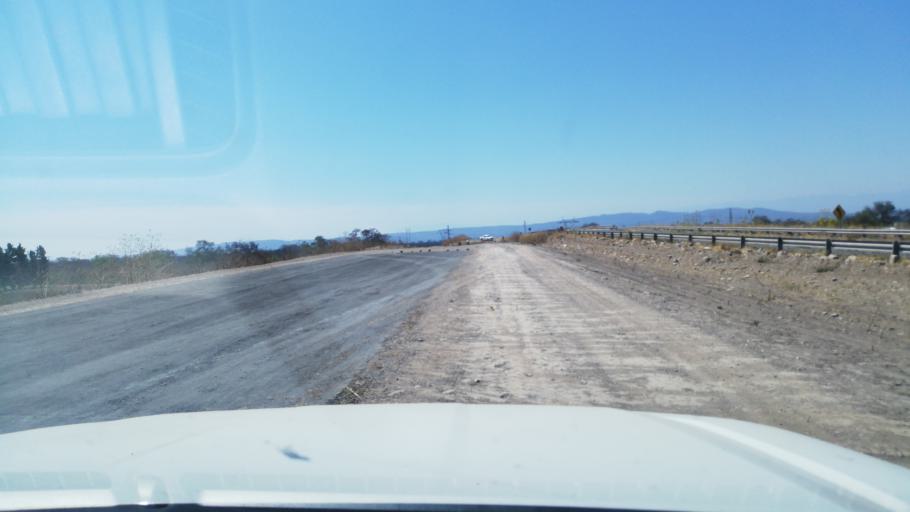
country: AR
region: Salta
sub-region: Departamento de General Guemes
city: General Martin Miguel de Guemes
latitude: -24.5248
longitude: -65.0730
